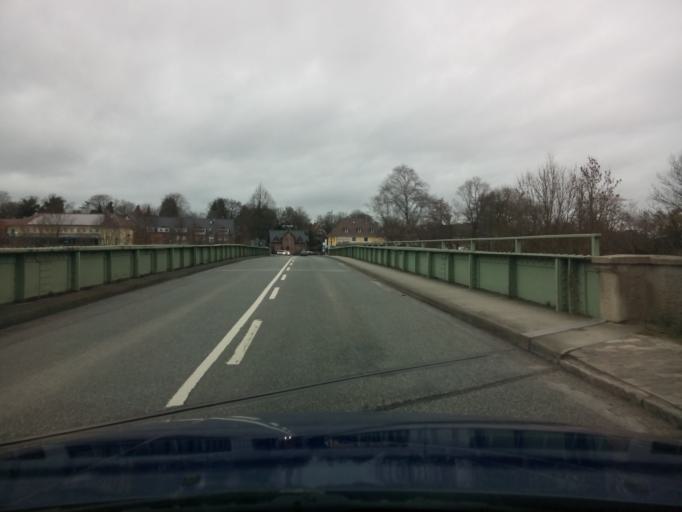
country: DE
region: Lower Saxony
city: Ritterhude
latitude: 53.1761
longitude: 8.7503
